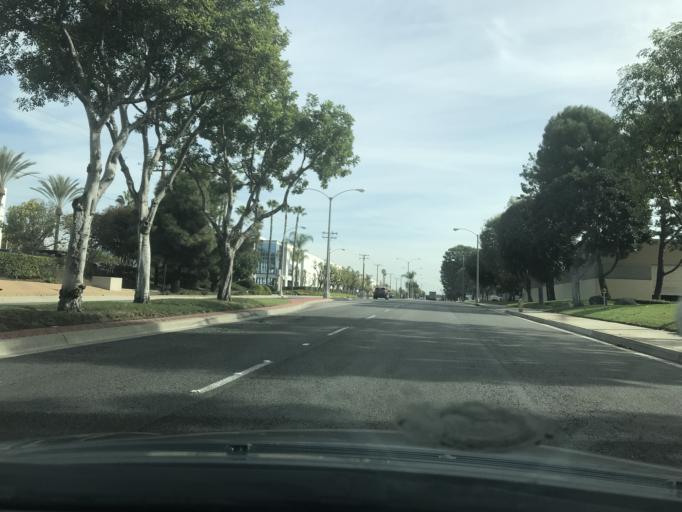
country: US
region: California
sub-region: Los Angeles County
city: Santa Fe Springs
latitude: 33.9352
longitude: -118.0596
